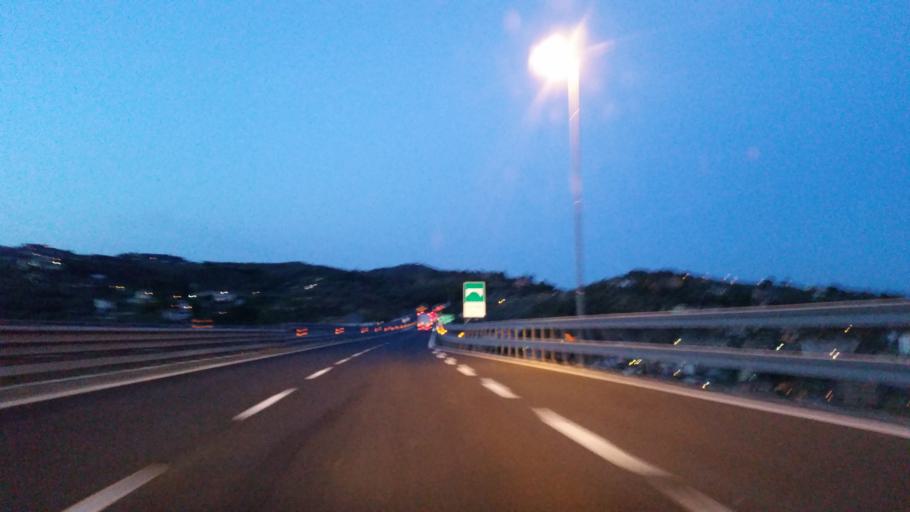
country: IT
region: Liguria
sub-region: Provincia di Imperia
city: Imperia
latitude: 43.8783
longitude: 7.9977
